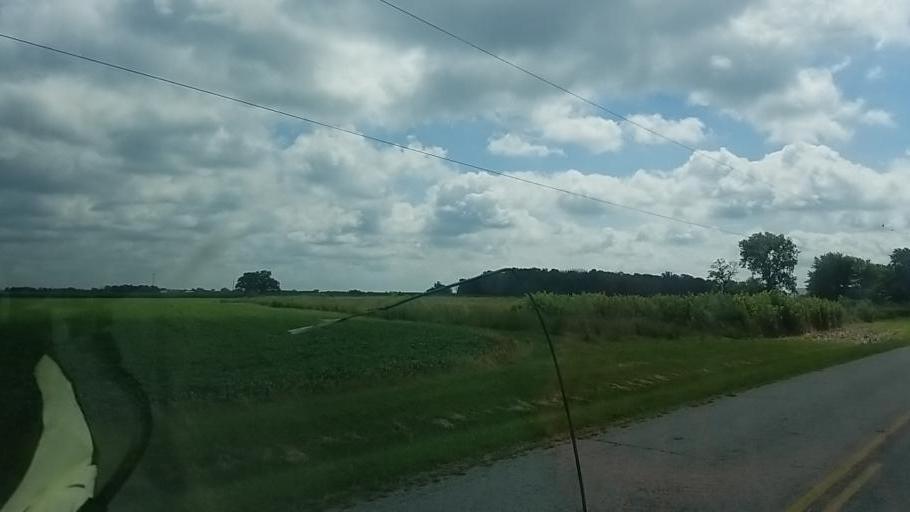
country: US
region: Ohio
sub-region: Madison County
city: Bethel
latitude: 39.7284
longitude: -83.4220
